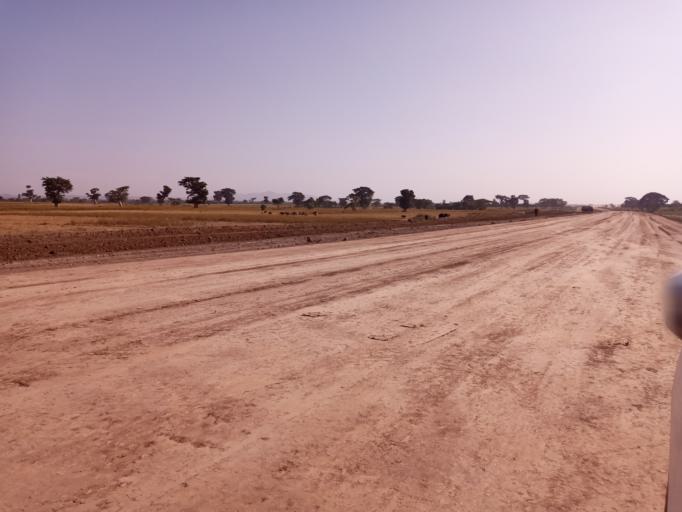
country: ET
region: Oromiya
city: Shashemene
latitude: 7.3030
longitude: 38.6173
